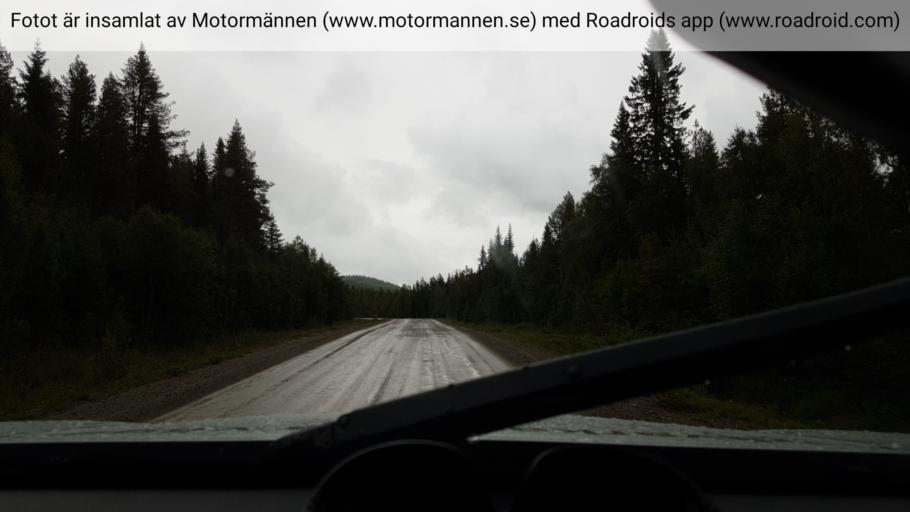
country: SE
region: Vaesterbotten
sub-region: Asele Kommun
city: Insjon
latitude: 64.8199
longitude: 17.4841
